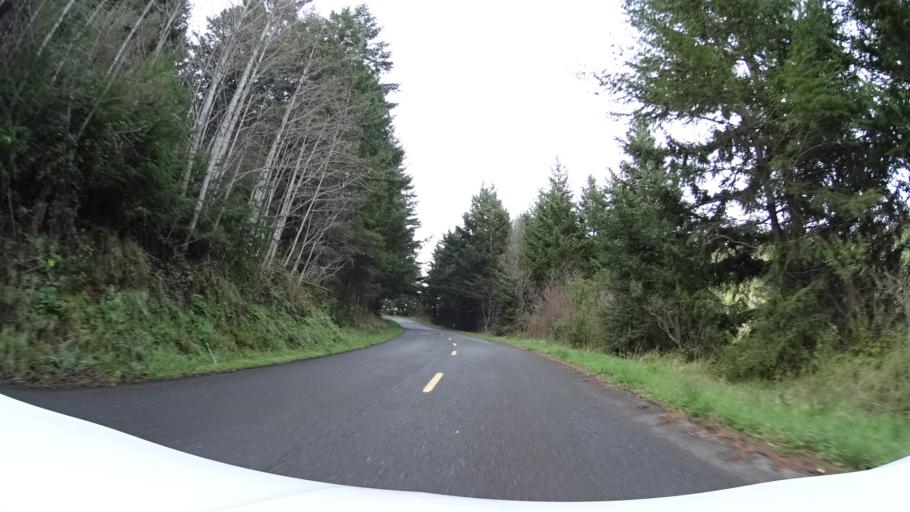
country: US
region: California
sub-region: Humboldt County
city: Ferndale
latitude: 40.3449
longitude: -124.3435
